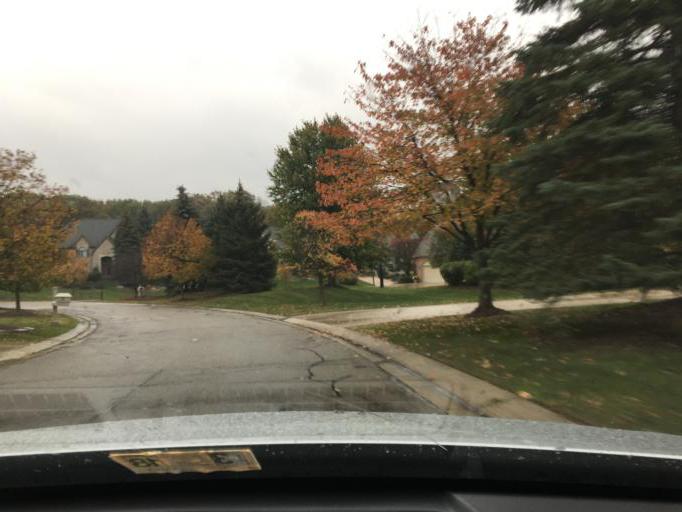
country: US
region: Michigan
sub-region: Oakland County
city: Auburn Hills
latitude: 42.7127
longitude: -83.2026
